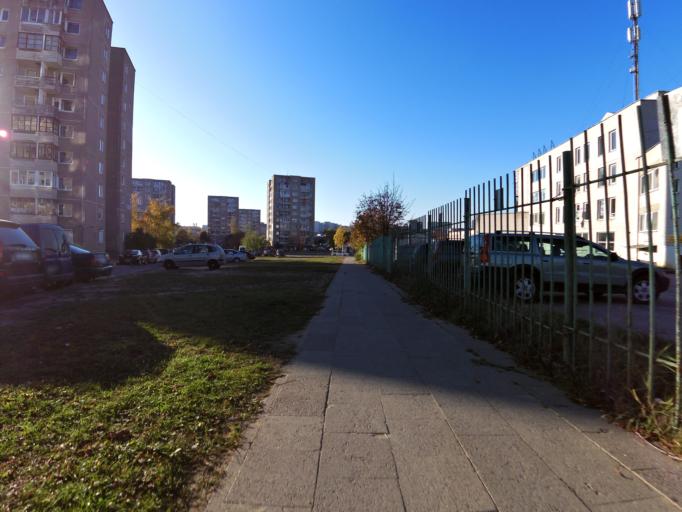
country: LT
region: Vilnius County
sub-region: Vilnius
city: Fabijoniskes
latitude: 54.7361
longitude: 25.2389
